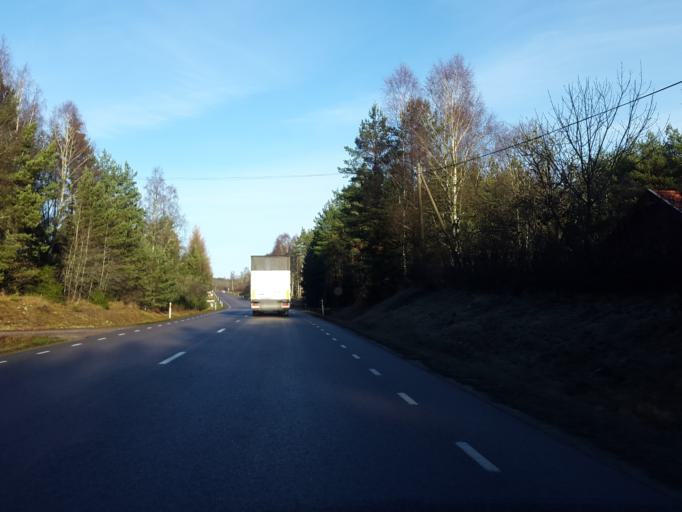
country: SE
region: Vaestra Goetaland
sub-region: Vargarda Kommun
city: Vargarda
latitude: 58.0048
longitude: 12.8143
